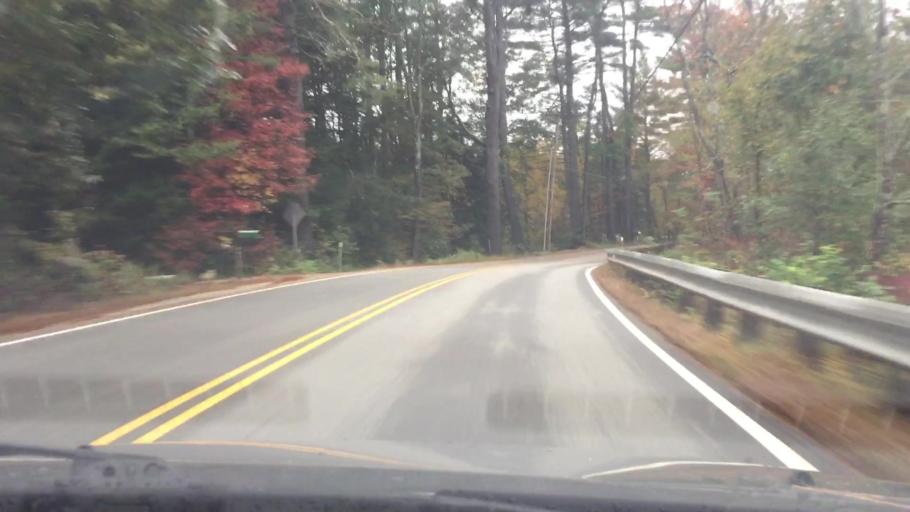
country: US
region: New Hampshire
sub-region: Cheshire County
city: Swanzey
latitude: 42.8478
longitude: -72.2795
